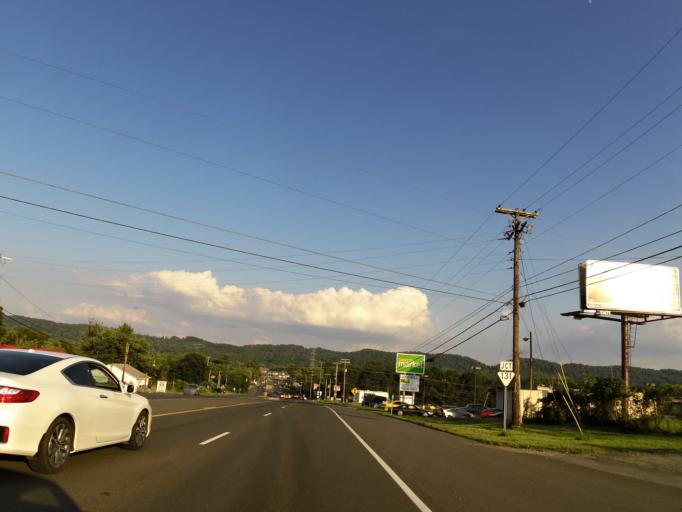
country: US
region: Tennessee
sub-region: Anderson County
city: Clinton
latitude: 36.0215
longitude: -84.0563
